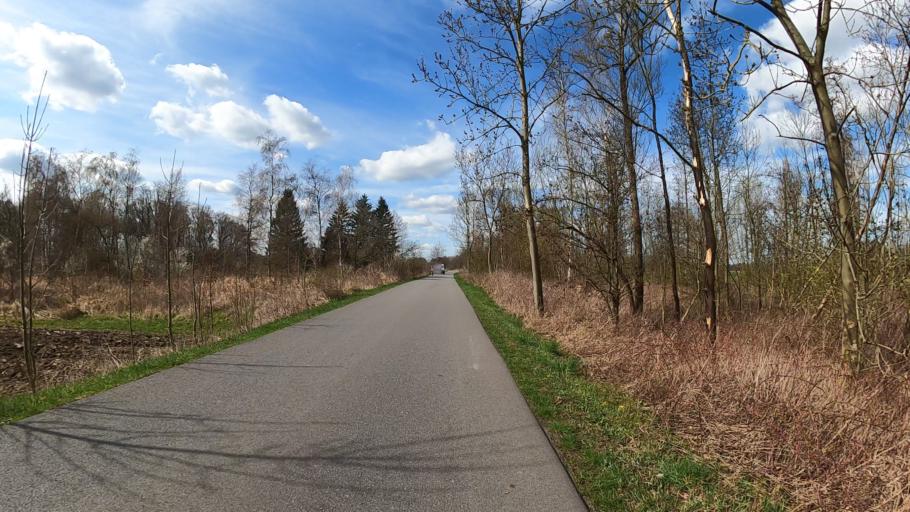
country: DE
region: Lower Saxony
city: Winsen
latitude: 53.4027
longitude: 10.2187
